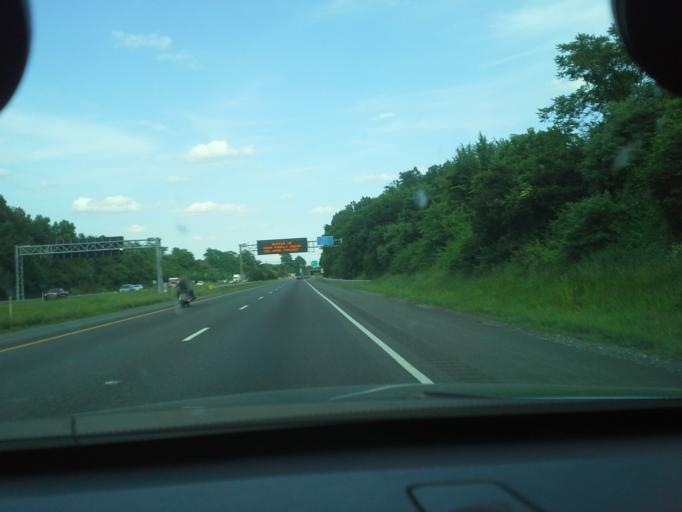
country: US
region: Maryland
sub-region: Frederick County
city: Ballenger Creek
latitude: 39.4029
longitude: -77.4541
